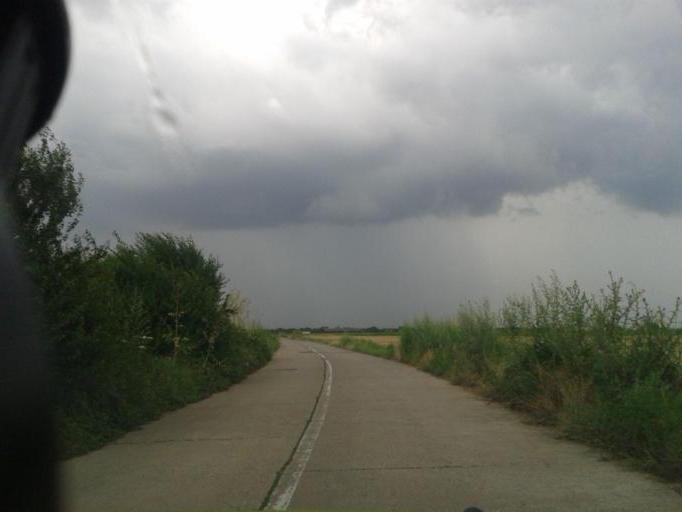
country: RO
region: Calarasi
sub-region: Comuna Belciugatele
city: Belciugatele
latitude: 44.5428
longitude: 26.4508
